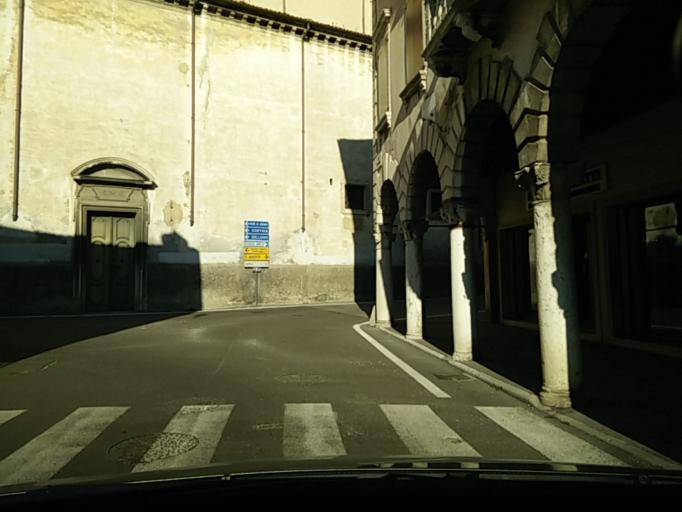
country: IT
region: Veneto
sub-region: Provincia di Treviso
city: Vittorio Veneto
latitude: 45.9995
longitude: 12.2911
